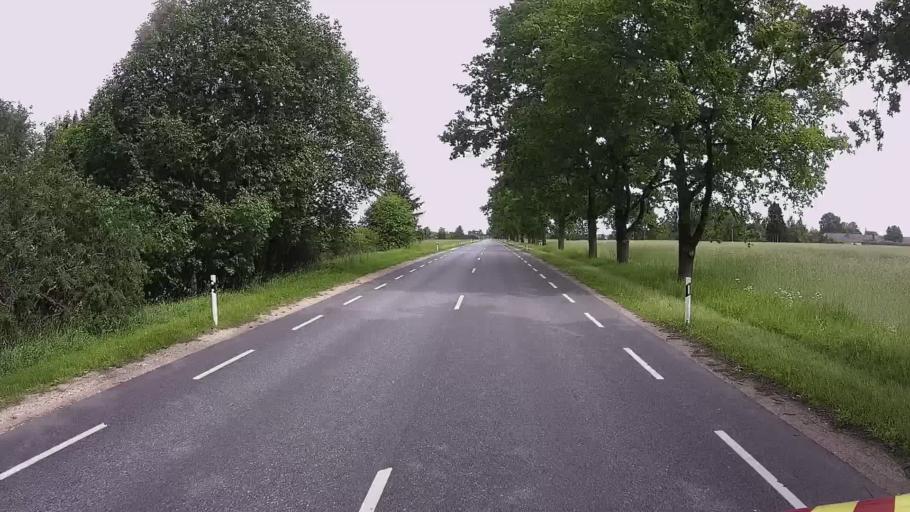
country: EE
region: Viljandimaa
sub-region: Karksi vald
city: Karksi-Nuia
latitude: 58.1223
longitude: 25.5827
